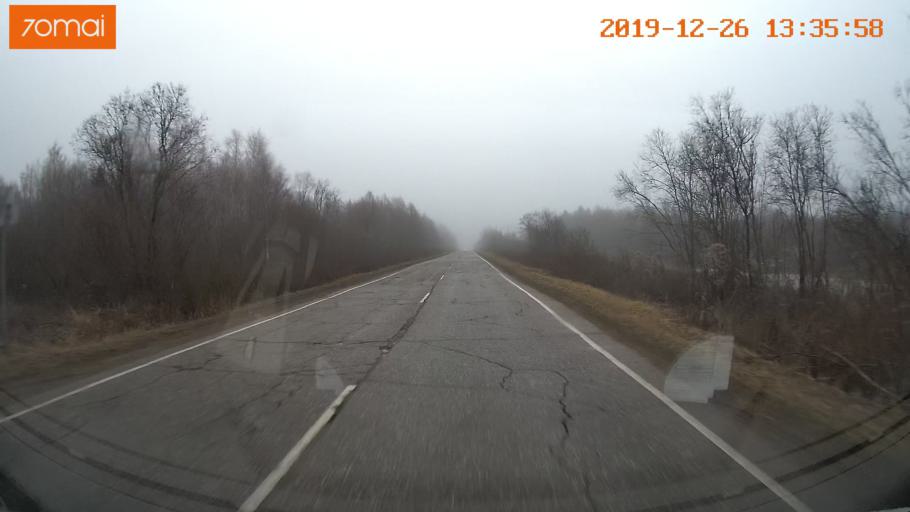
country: RU
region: Vologda
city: Sheksna
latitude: 58.7879
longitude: 38.3480
